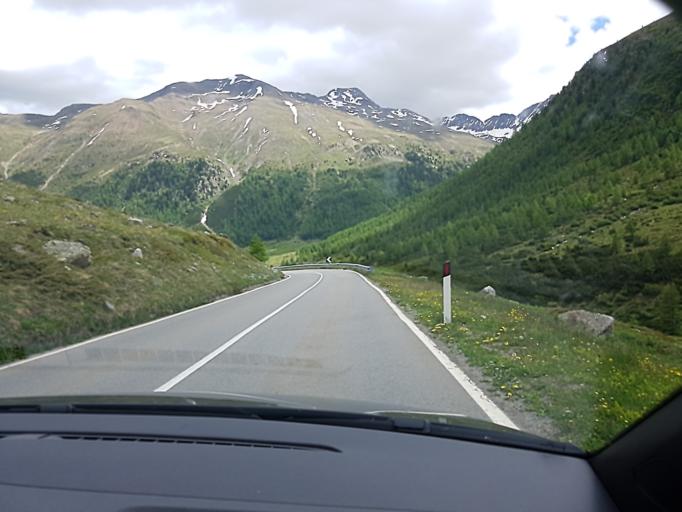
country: IT
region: Lombardy
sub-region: Provincia di Sondrio
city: Livigno
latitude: 46.4617
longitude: 10.0786
